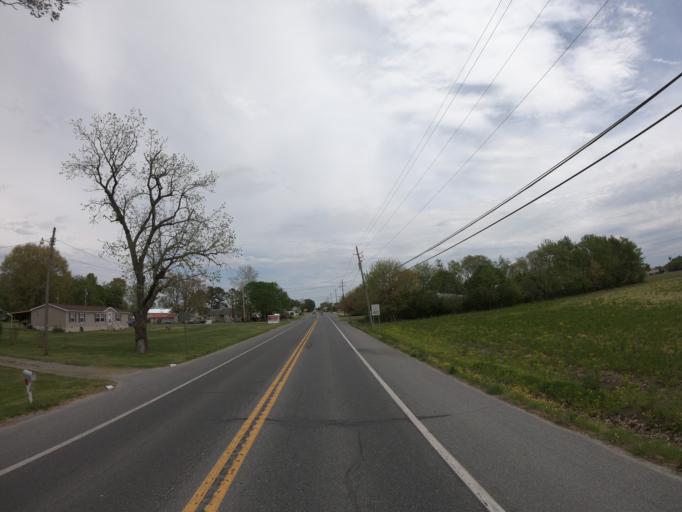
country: US
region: Delaware
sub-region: Sussex County
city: Milton
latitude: 38.7874
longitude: -75.3247
